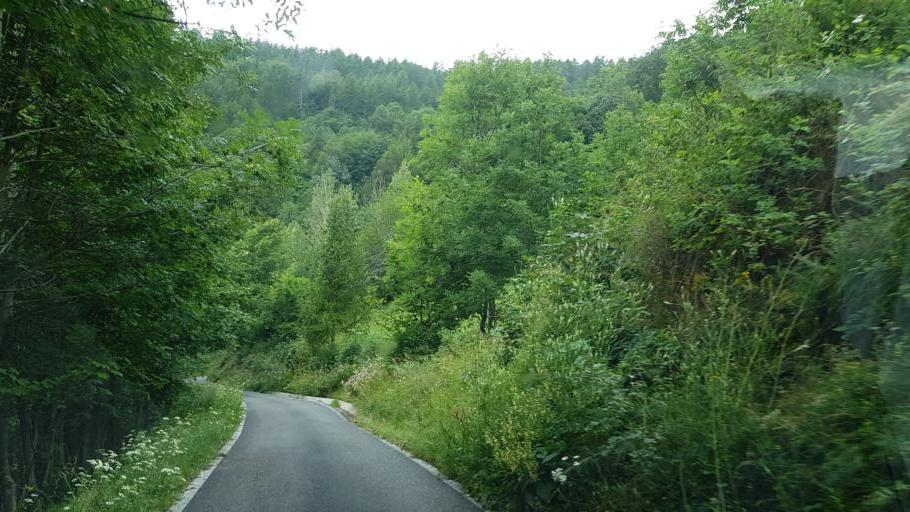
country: IT
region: Piedmont
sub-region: Provincia di Cuneo
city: Stroppo
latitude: 44.5136
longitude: 7.1138
